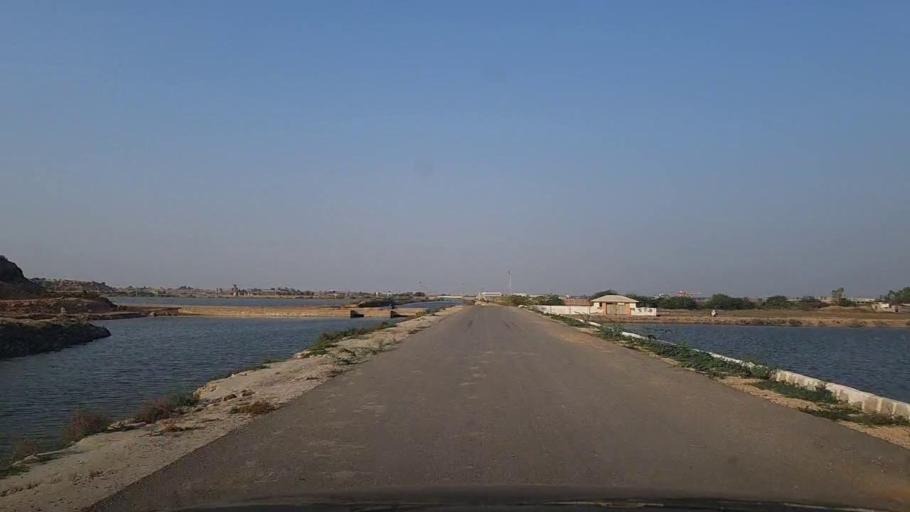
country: PK
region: Sindh
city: Thatta
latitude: 24.7442
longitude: 67.9069
